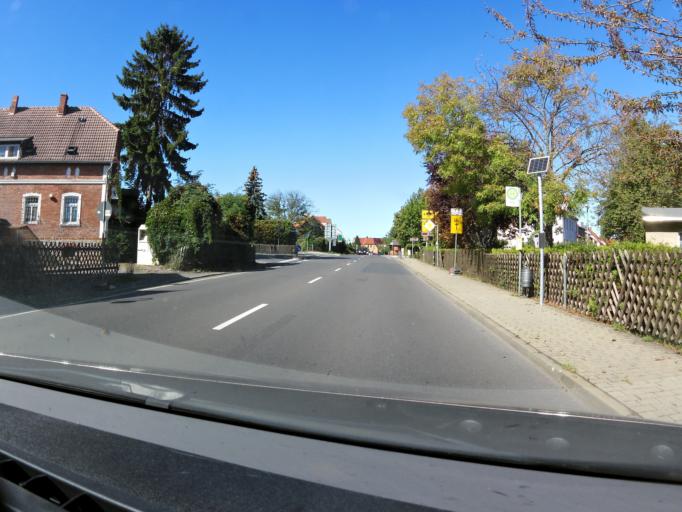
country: DE
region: Saxony-Anhalt
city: Bad Suderode
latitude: 51.7319
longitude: 11.1259
